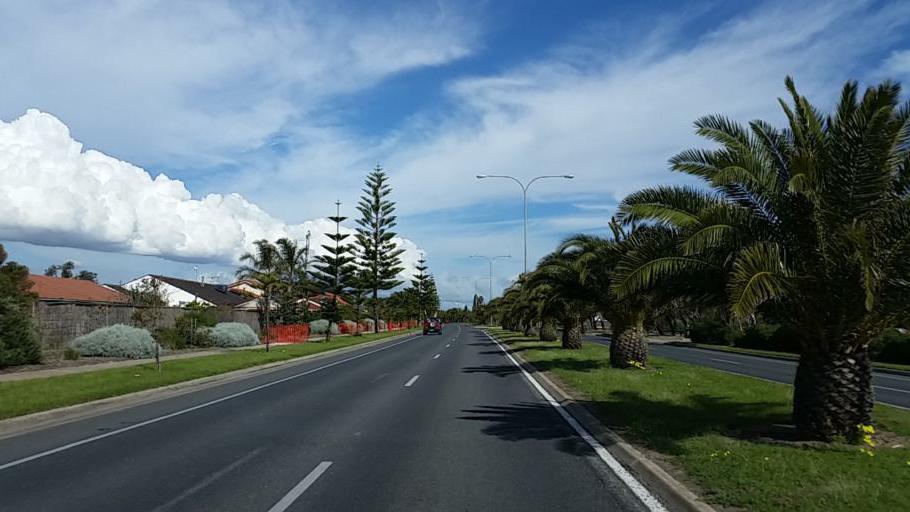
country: AU
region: South Australia
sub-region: Charles Sturt
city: West Lakes Shore
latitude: -34.8796
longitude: 138.4852
